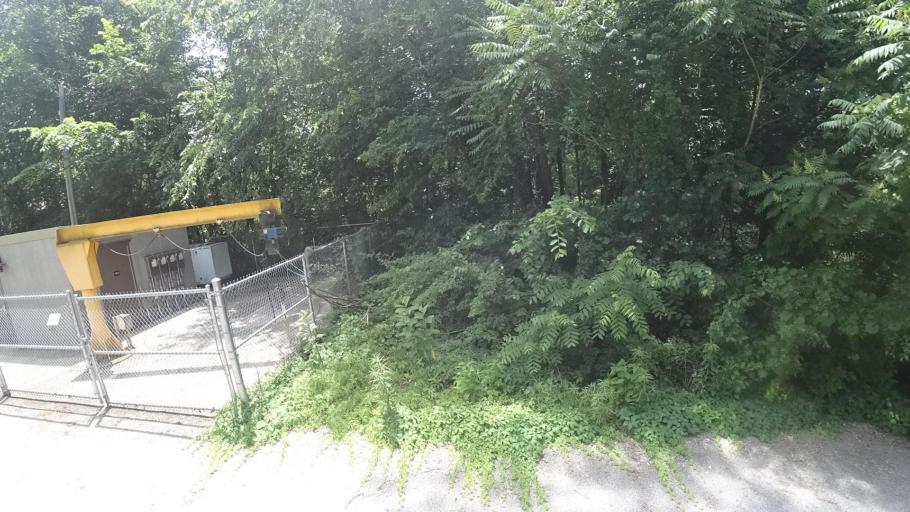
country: US
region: Indiana
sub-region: Porter County
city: Porter
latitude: 41.6208
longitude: -87.0744
